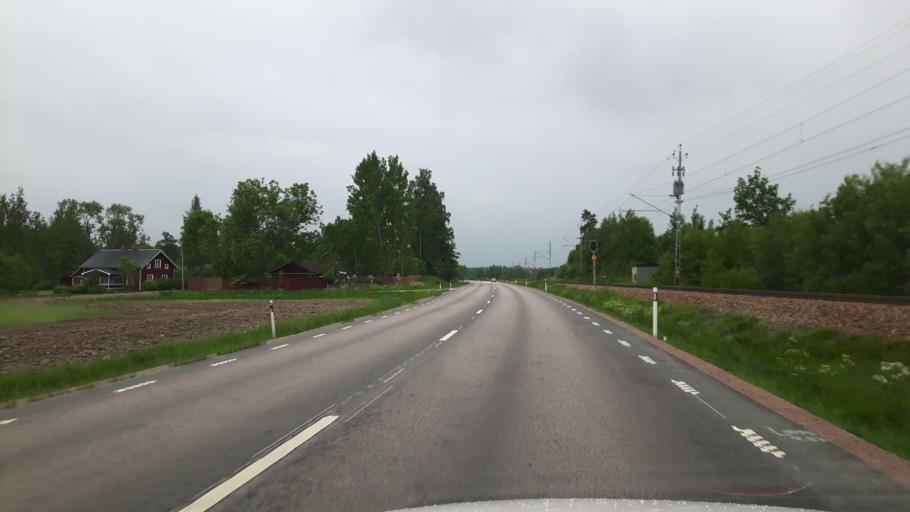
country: SE
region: Vaestmanland
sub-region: Kopings Kommun
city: Koping
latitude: 59.4744
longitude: 15.9694
